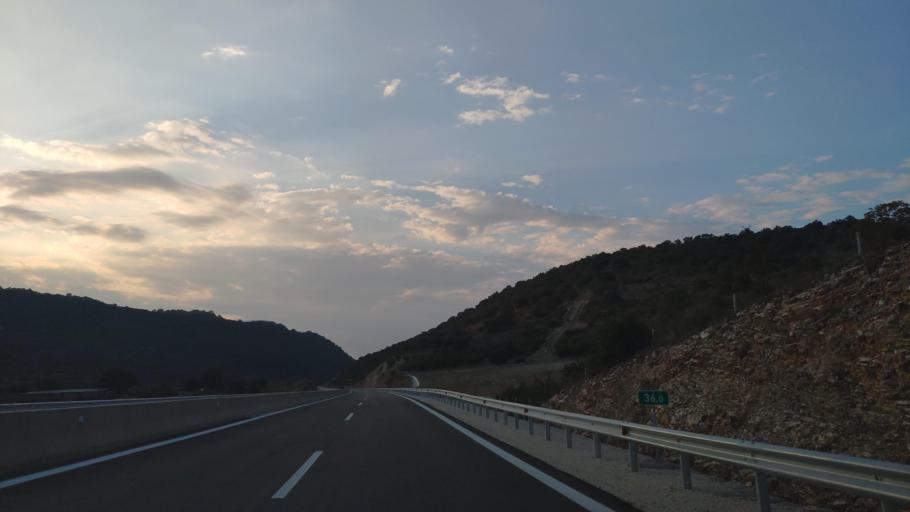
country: GR
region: West Greece
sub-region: Nomos Aitolias kai Akarnanias
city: Katouna
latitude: 38.8447
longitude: 21.1021
